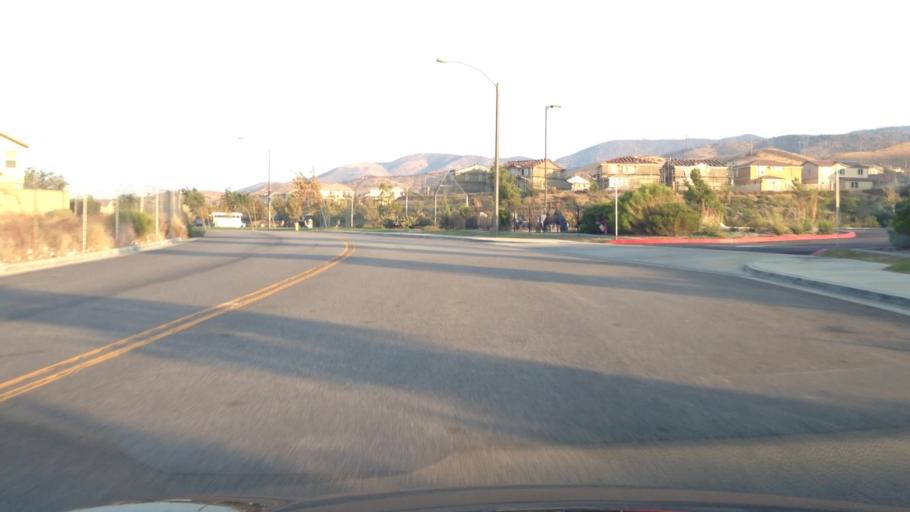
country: US
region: California
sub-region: Los Angeles County
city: Desert View Highlands
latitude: 34.5654
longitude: -118.1795
